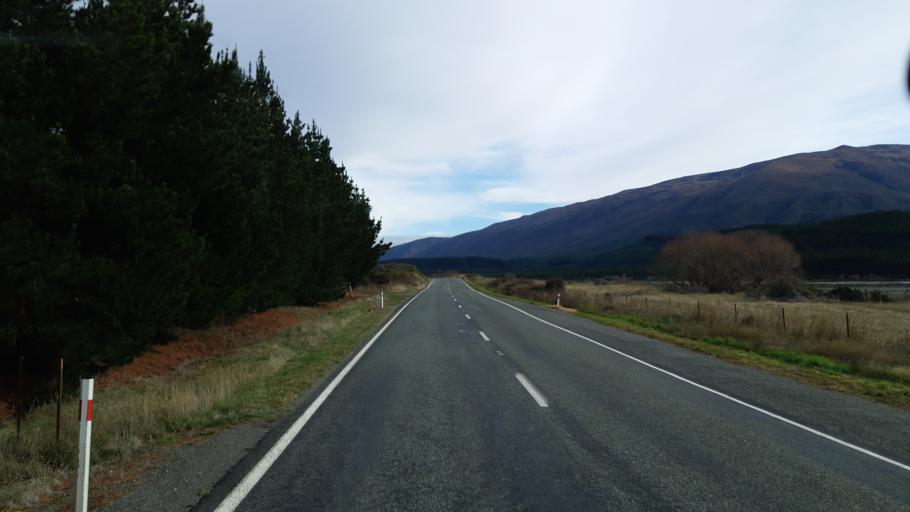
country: NZ
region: Tasman
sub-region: Tasman District
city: Wakefield
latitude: -41.6917
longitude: 173.1482
